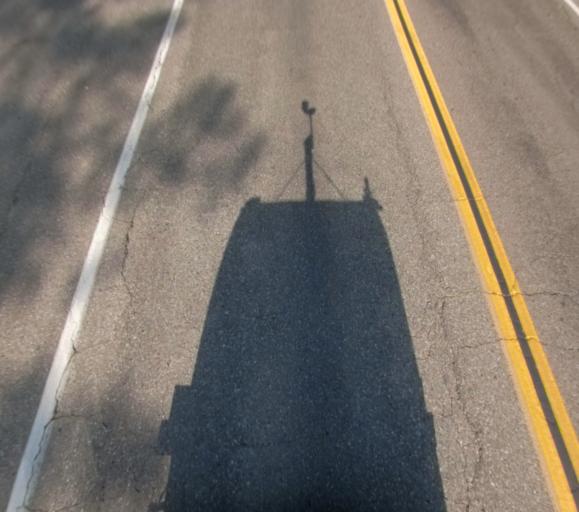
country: US
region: California
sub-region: Fresno County
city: Auberry
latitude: 37.2301
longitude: -119.4988
